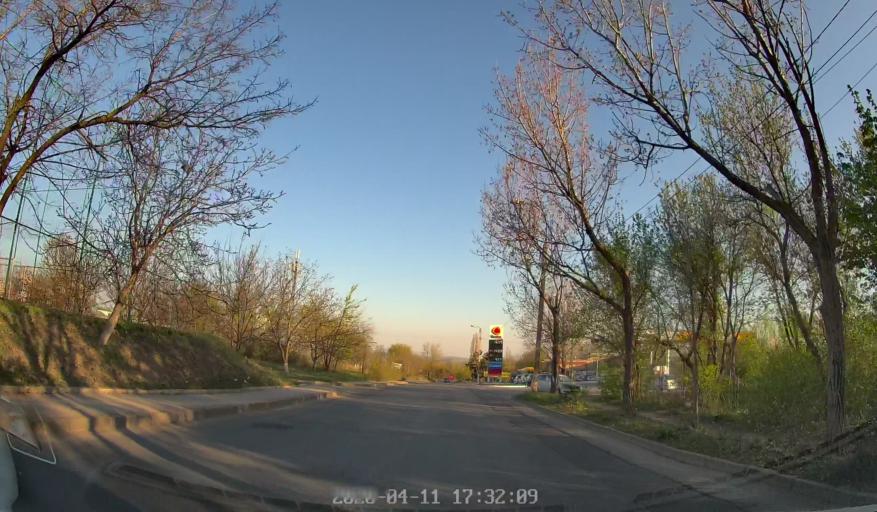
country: MD
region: Laloveni
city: Ialoveni
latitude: 46.9948
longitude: 28.7863
